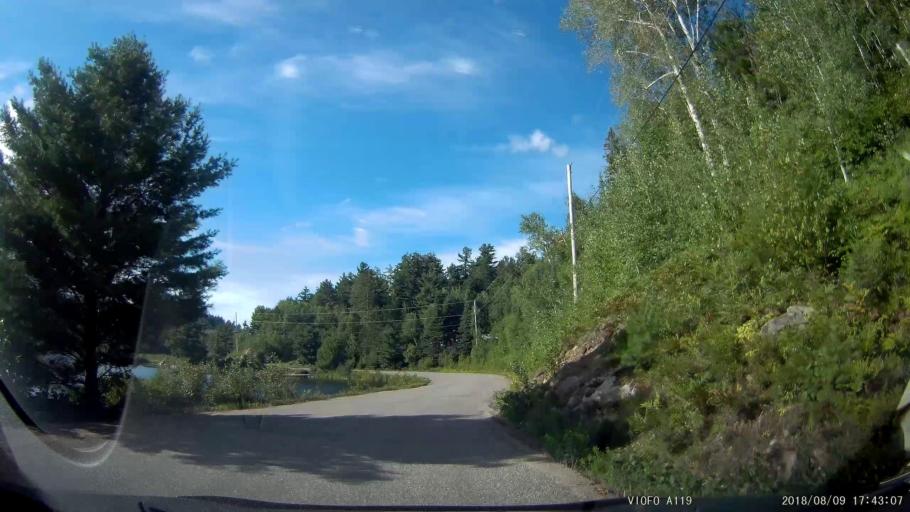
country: CA
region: Ontario
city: Rayside-Balfour
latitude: 46.6056
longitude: -81.5266
